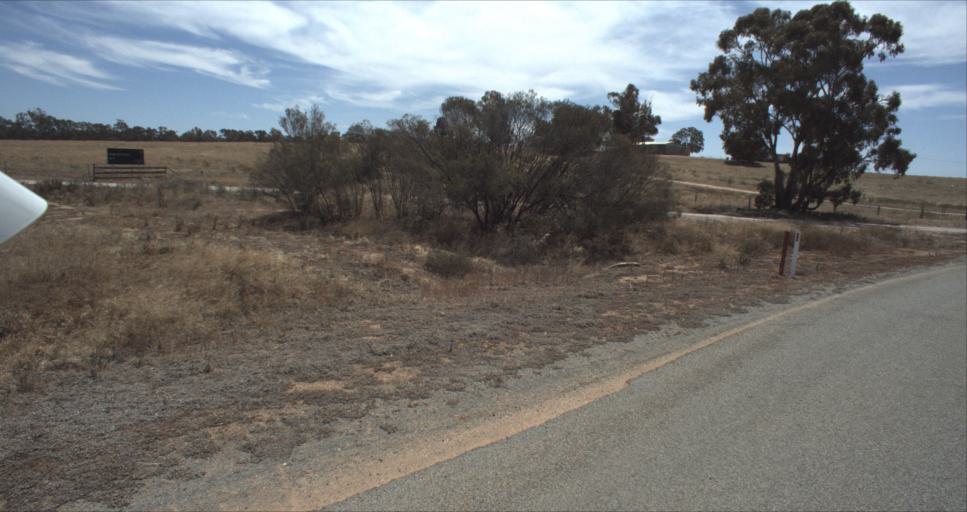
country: AU
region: New South Wales
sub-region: Leeton
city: Leeton
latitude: -34.6744
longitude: 146.4330
